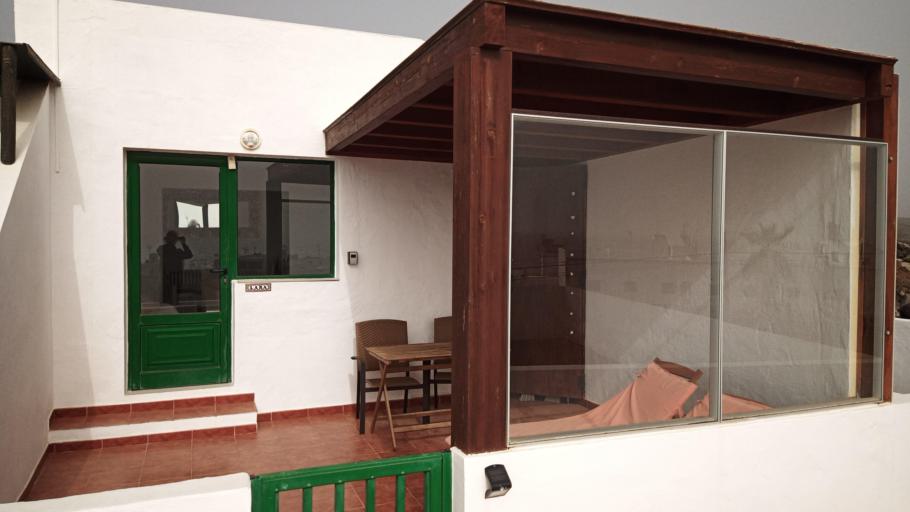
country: ES
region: Canary Islands
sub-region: Provincia de Las Palmas
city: Haria
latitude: 29.1424
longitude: -13.4521
